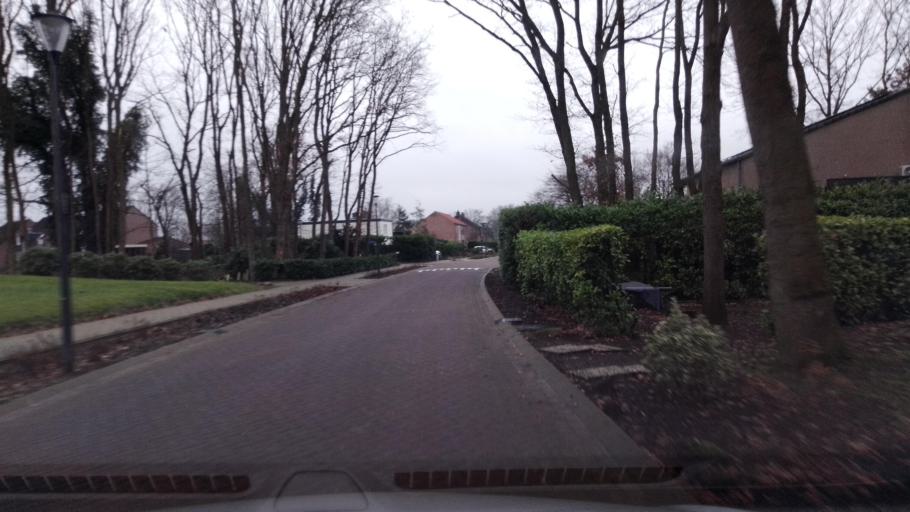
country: NL
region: Limburg
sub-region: Gemeente Bergen
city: Wellerlooi
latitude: 51.5344
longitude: 6.1038
